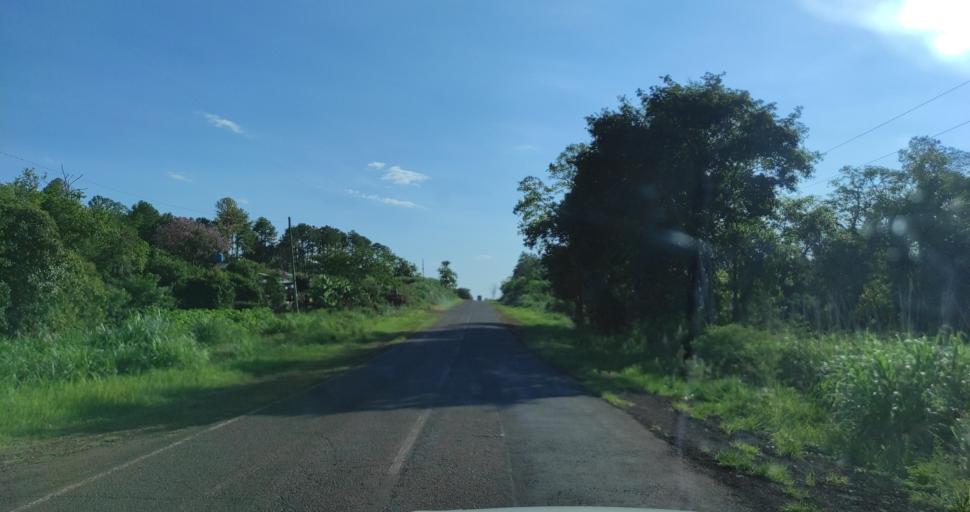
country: AR
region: Misiones
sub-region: Departamento de Eldorado
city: Eldorado
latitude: -26.3809
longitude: -54.3400
